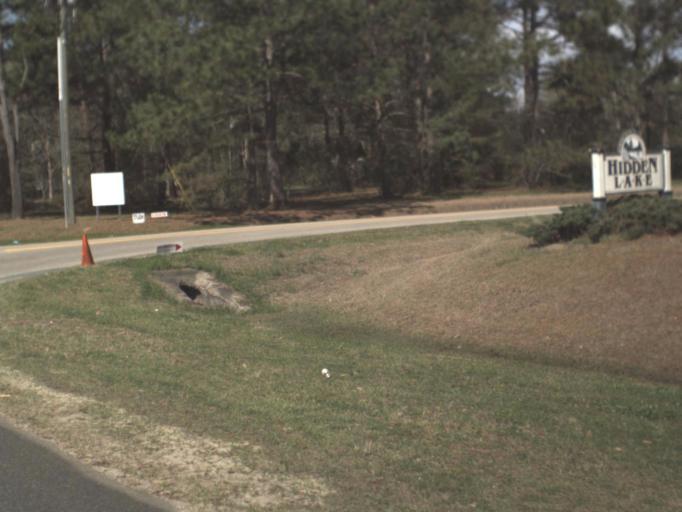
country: US
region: Florida
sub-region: Gadsden County
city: Havana
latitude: 30.6167
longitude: -84.4439
